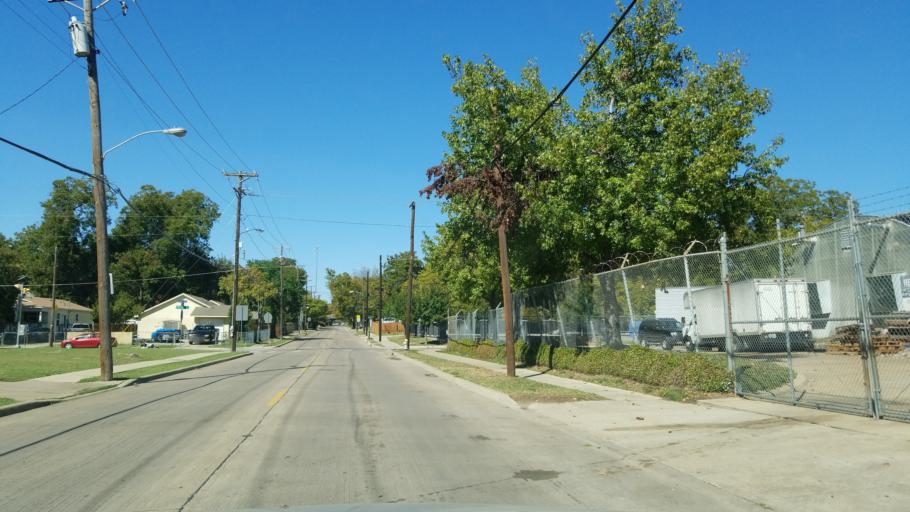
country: US
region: Texas
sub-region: Dallas County
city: Dallas
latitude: 32.7878
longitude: -96.7552
